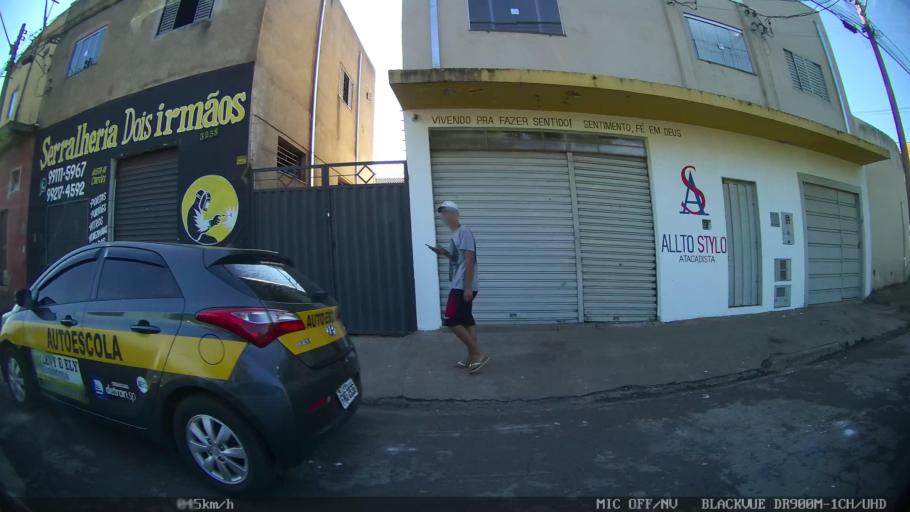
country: BR
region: Sao Paulo
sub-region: Franca
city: Franca
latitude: -20.4851
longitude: -47.4221
